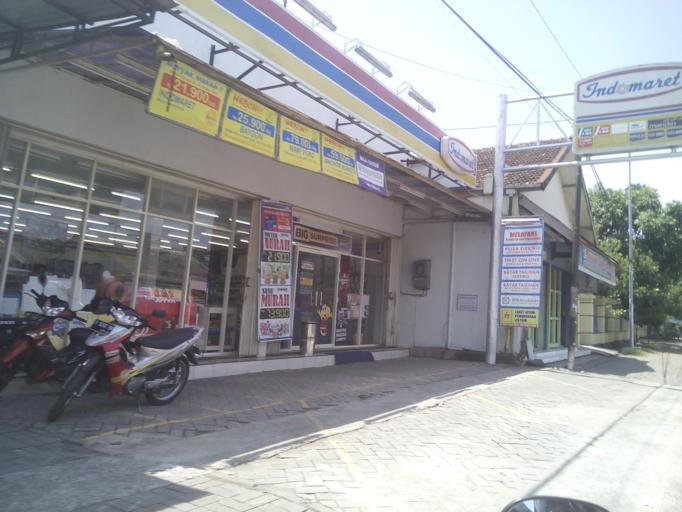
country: ID
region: East Java
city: Kloncing
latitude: -8.1889
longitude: 113.7208
